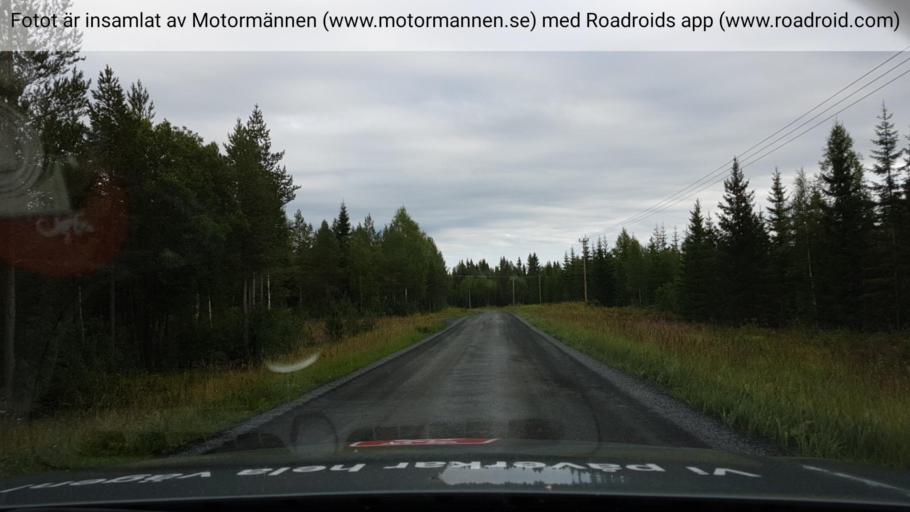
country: SE
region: Jaemtland
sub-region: Krokoms Kommun
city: Valla
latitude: 63.3440
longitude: 14.0038
